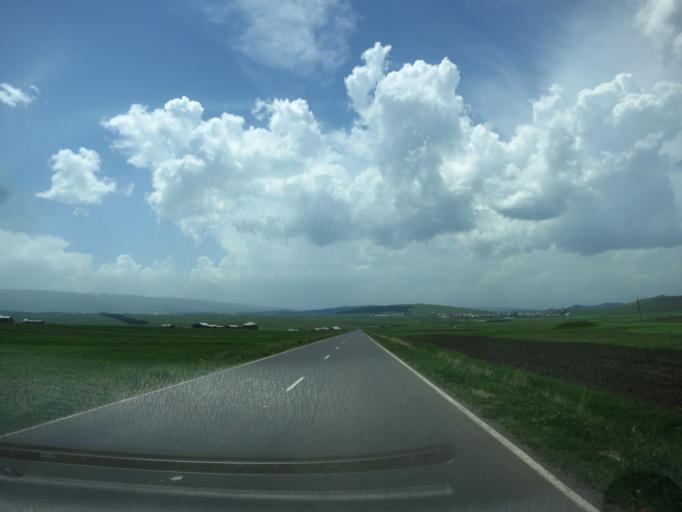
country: GE
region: Samtskhe-Javakheti
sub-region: Ninotsminda
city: Ninotsminda
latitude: 41.2953
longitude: 43.6557
